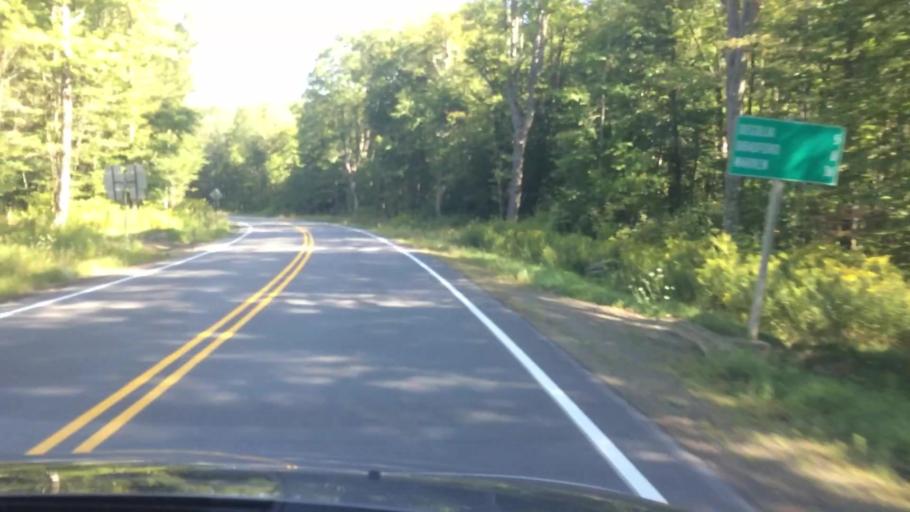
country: US
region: Pennsylvania
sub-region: McKean County
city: Bradford
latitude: 41.8794
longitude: -78.5770
